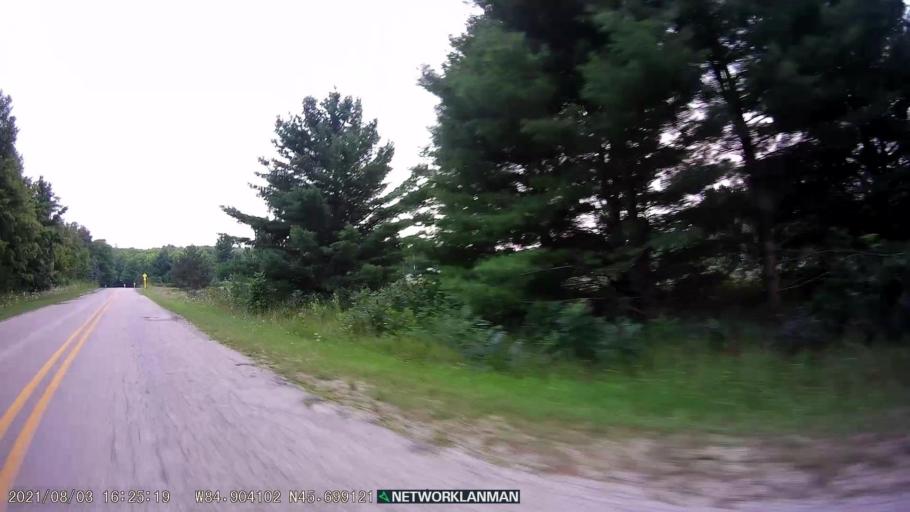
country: US
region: Michigan
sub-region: Mackinac County
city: Saint Ignace
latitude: 45.6984
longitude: -84.9045
